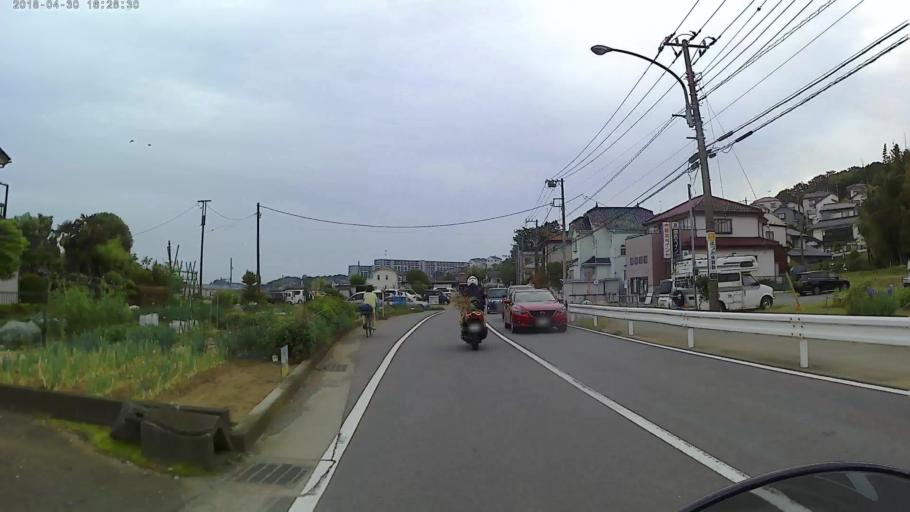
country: JP
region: Kanagawa
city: Zama
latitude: 35.4633
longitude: 139.4072
